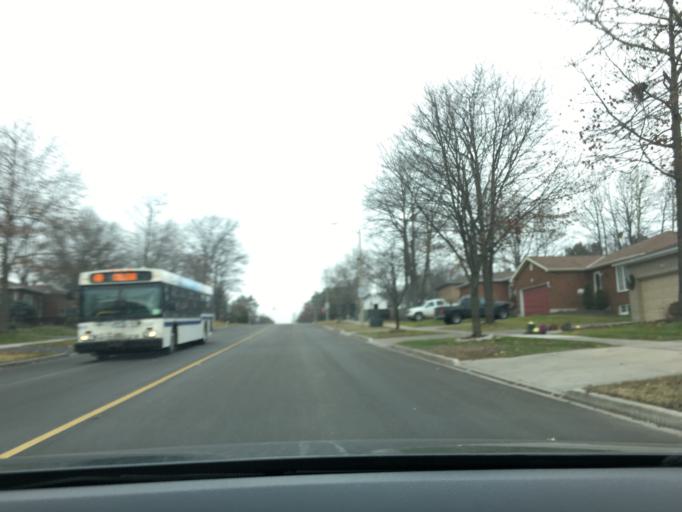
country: CA
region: Ontario
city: Barrie
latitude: 44.3889
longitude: -79.7202
